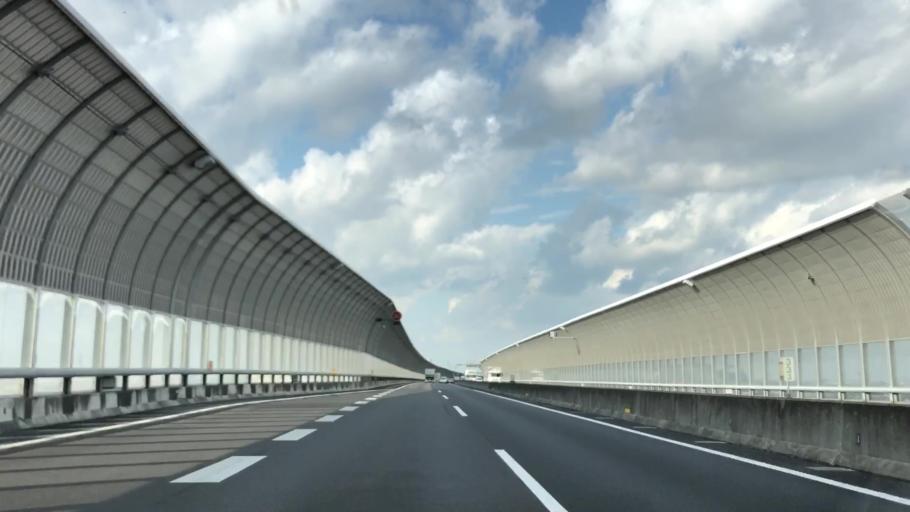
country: JP
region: Chiba
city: Matsudo
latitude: 35.8056
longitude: 139.8768
